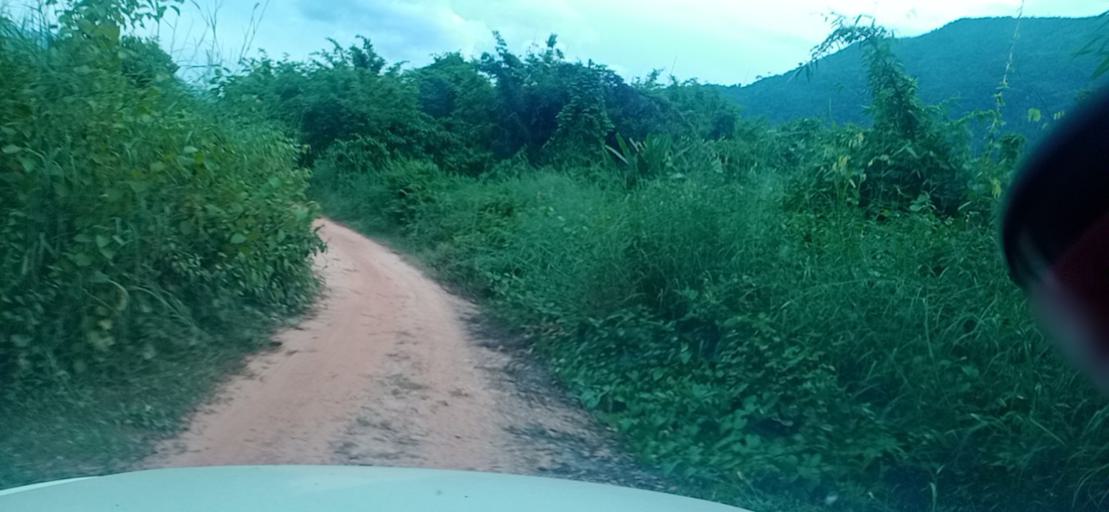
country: TH
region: Changwat Bueng Kan
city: Pak Khat
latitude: 18.5619
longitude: 103.2884
